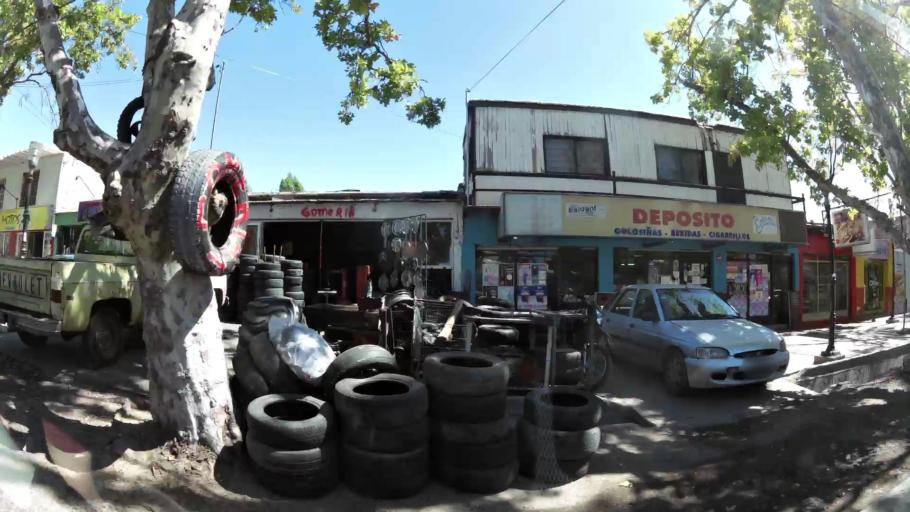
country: AR
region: Mendoza
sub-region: Departamento de Godoy Cruz
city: Godoy Cruz
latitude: -32.9562
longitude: -68.8507
